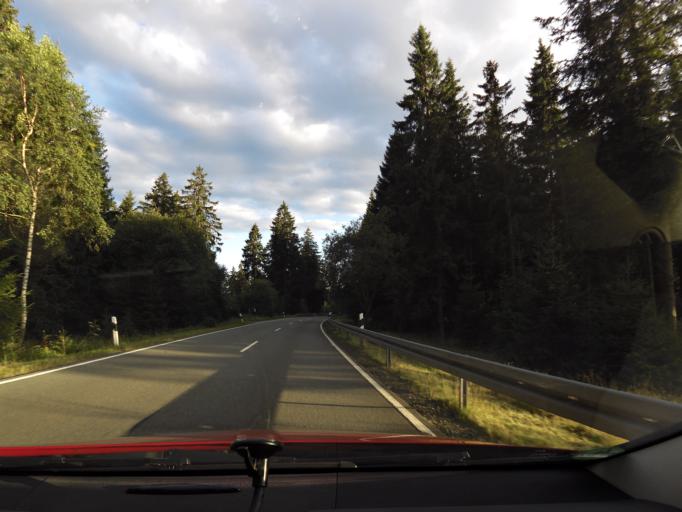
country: DE
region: Lower Saxony
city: Sankt Andreasberg
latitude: 51.7346
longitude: 10.5239
